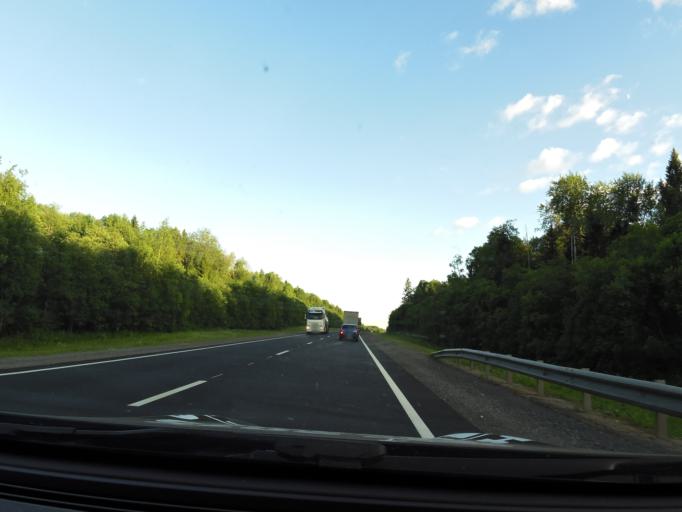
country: RU
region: Vologda
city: Gryazovets
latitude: 58.9393
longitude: 40.1748
